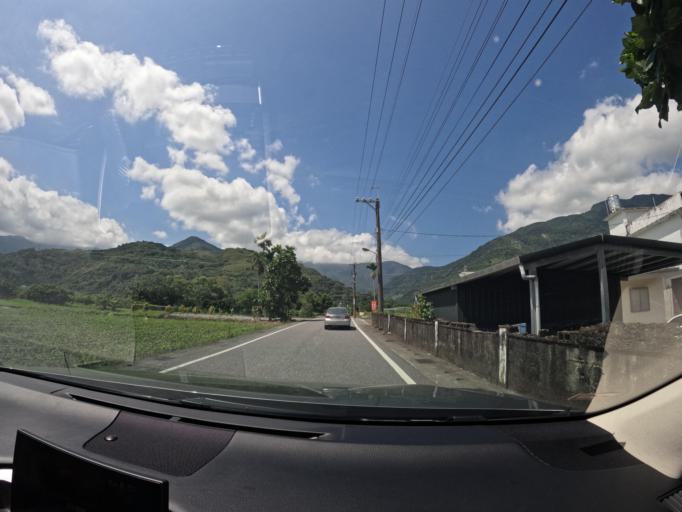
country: TW
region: Taiwan
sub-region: Hualien
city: Hualian
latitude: 23.7137
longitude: 121.4175
